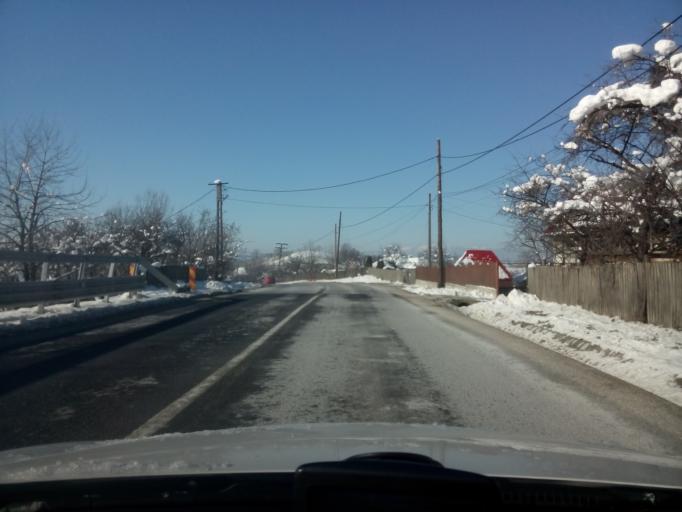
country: RO
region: Arges
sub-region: Comuna Moraresti
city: Moraresti
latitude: 45.0183
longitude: 24.5303
